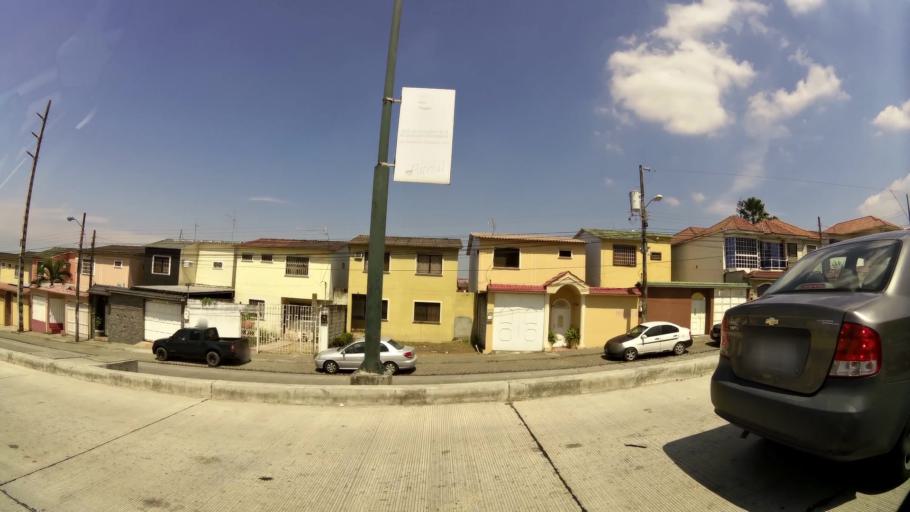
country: EC
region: Guayas
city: Eloy Alfaro
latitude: -2.1094
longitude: -79.9075
